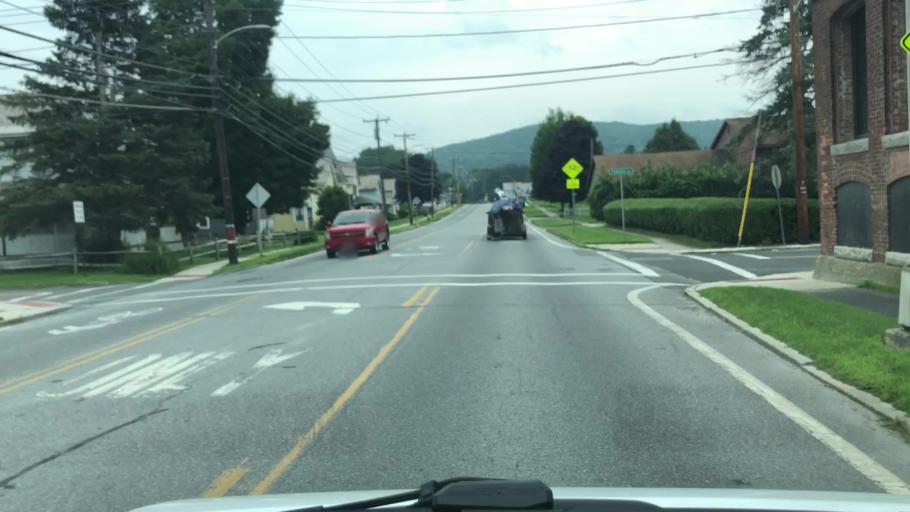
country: US
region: Massachusetts
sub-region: Berkshire County
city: North Adams
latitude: 42.6984
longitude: -73.1508
